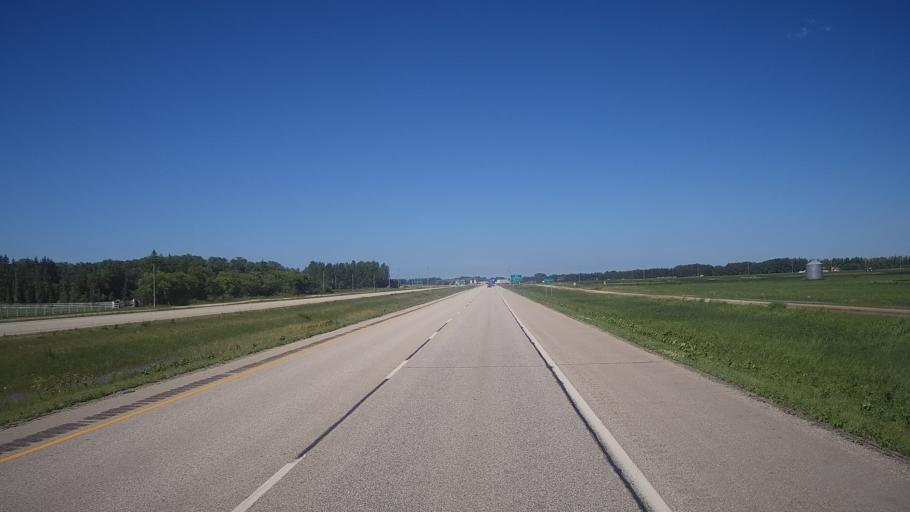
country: CA
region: Manitoba
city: Portage la Prairie
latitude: 49.9601
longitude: -98.2488
